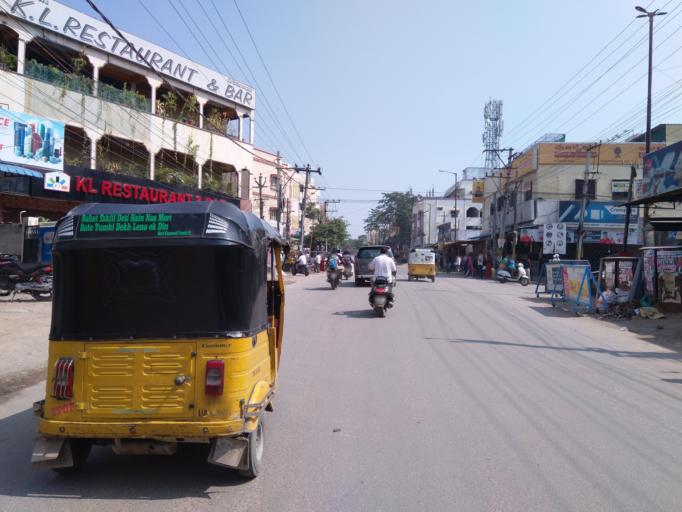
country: IN
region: Telangana
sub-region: Rangareddi
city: Kukatpalli
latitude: 17.5002
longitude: 78.4156
